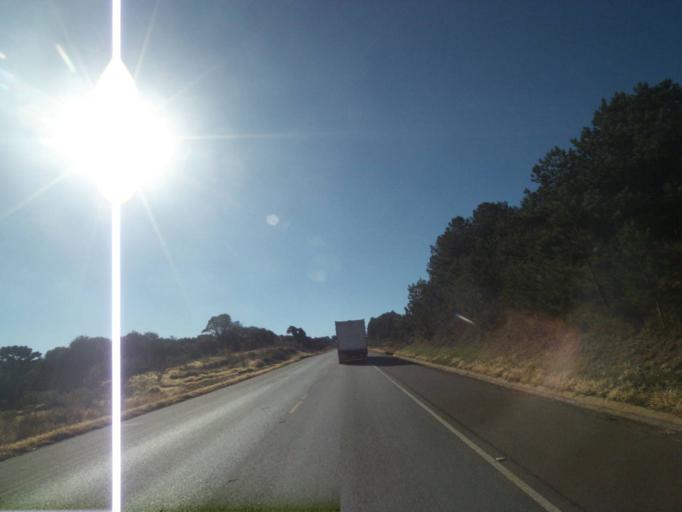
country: BR
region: Parana
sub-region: Tibagi
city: Tibagi
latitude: -24.5341
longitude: -50.4474
